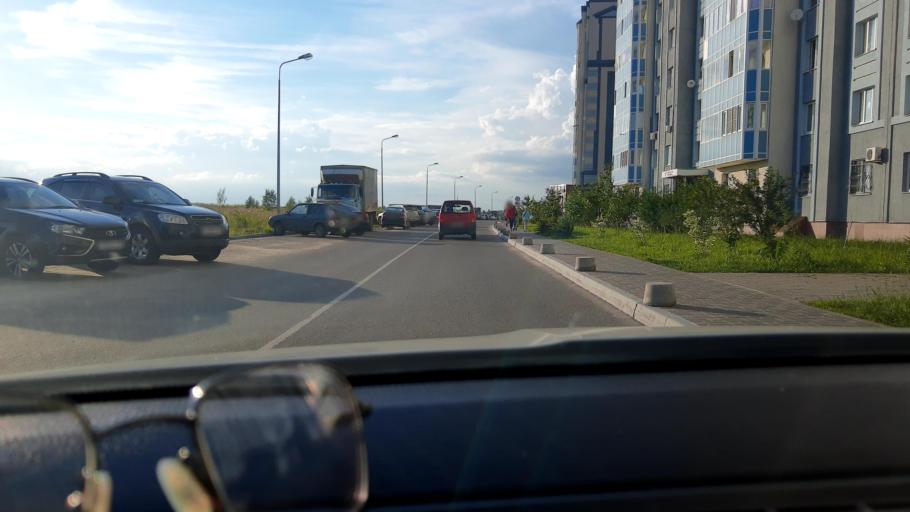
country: RU
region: Moskovskaya
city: Vostryakovo
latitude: 55.4018
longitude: 37.7670
